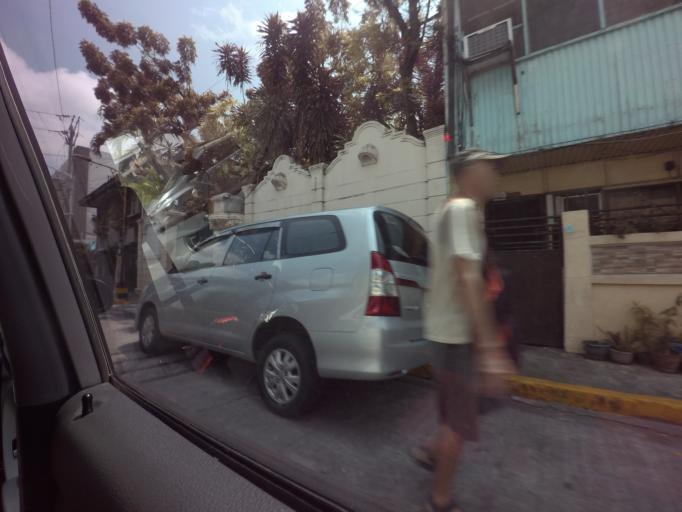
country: PH
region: Metro Manila
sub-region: City of Manila
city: Quiapo
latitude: 14.5908
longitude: 121.0030
